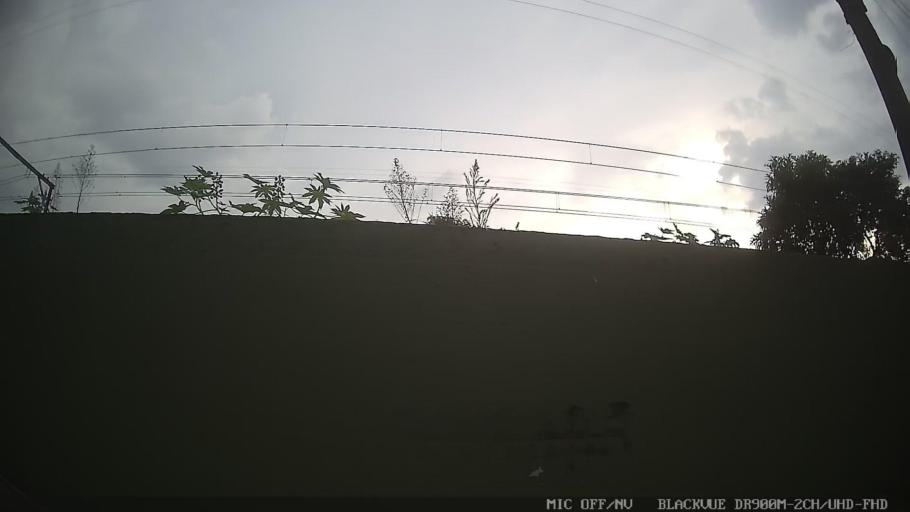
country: BR
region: Sao Paulo
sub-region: Ribeirao Pires
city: Ribeirao Pires
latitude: -23.7087
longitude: -46.4193
